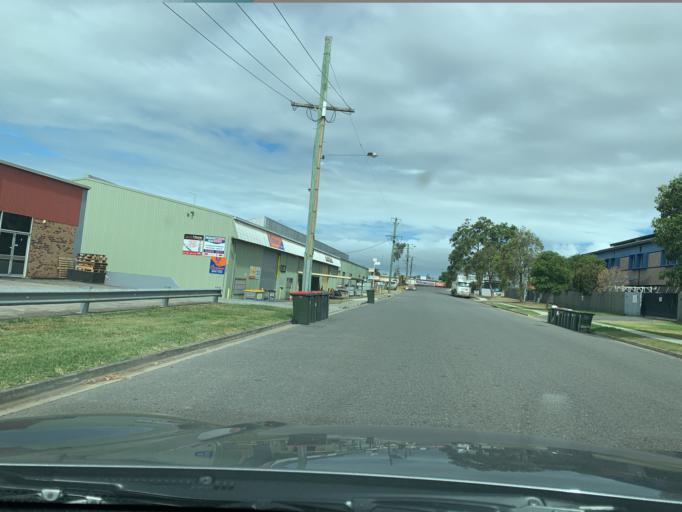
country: AU
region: Queensland
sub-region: Brisbane
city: Wynnum West
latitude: -27.4785
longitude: 153.1408
